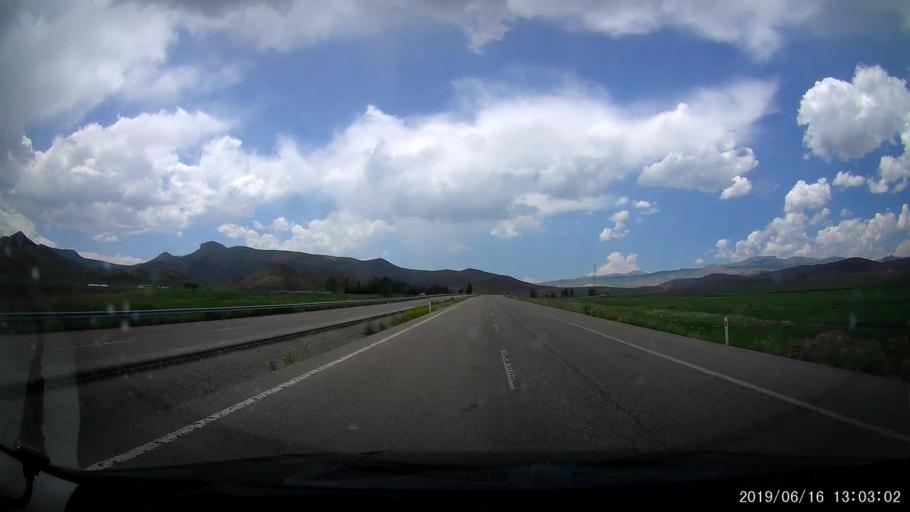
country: TR
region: Agri
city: Sulucem
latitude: 39.5782
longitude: 43.7999
